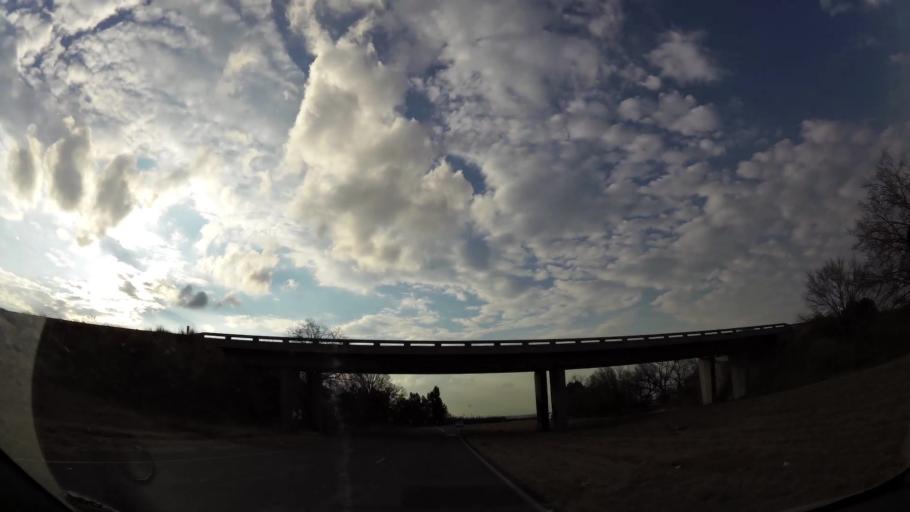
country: ZA
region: Orange Free State
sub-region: Fezile Dabi District Municipality
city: Sasolburg
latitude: -26.7868
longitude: 27.8248
